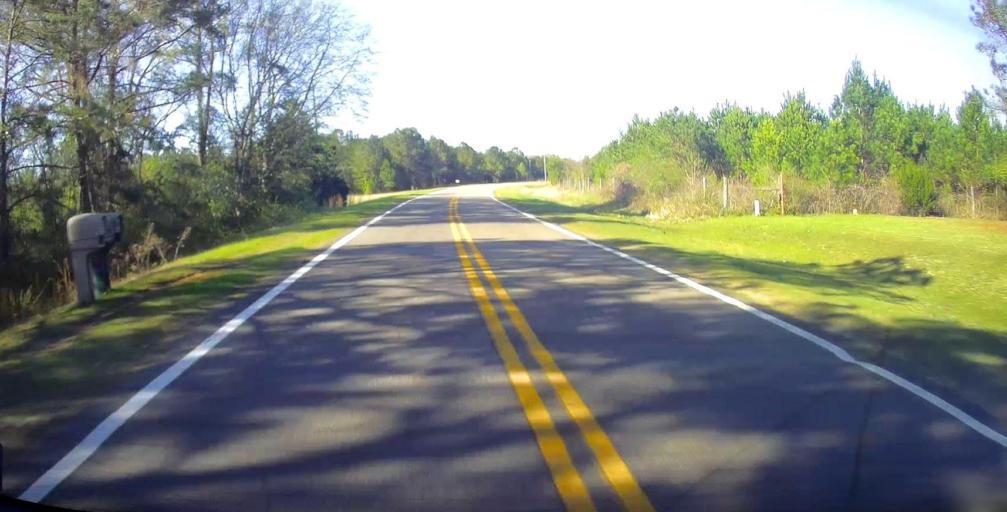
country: US
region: Georgia
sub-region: Peach County
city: Fort Valley
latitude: 32.5886
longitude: -83.9899
